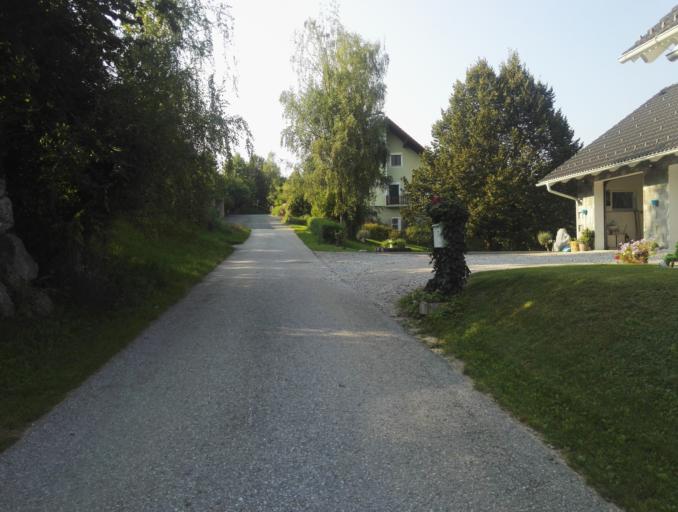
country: AT
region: Styria
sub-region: Politischer Bezirk Graz-Umgebung
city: Sankt Oswald bei Plankenwarth
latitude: 47.0879
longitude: 15.2674
